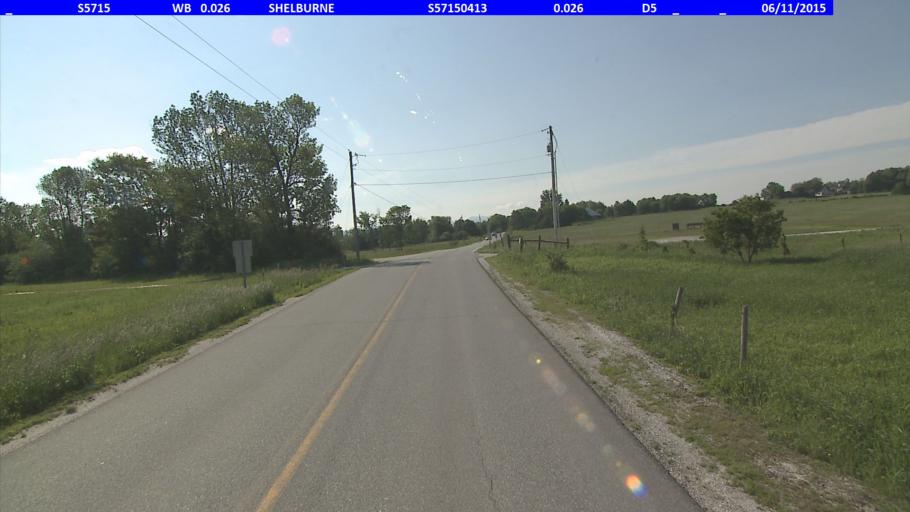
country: US
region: Vermont
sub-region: Chittenden County
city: Hinesburg
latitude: 44.3629
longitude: -73.1622
